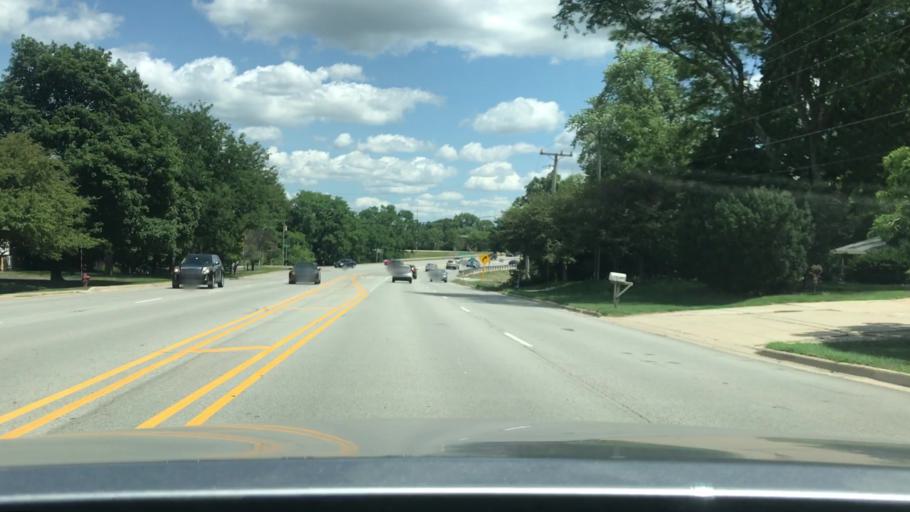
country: US
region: Illinois
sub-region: DuPage County
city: Woodridge
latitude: 41.7707
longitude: -88.0494
